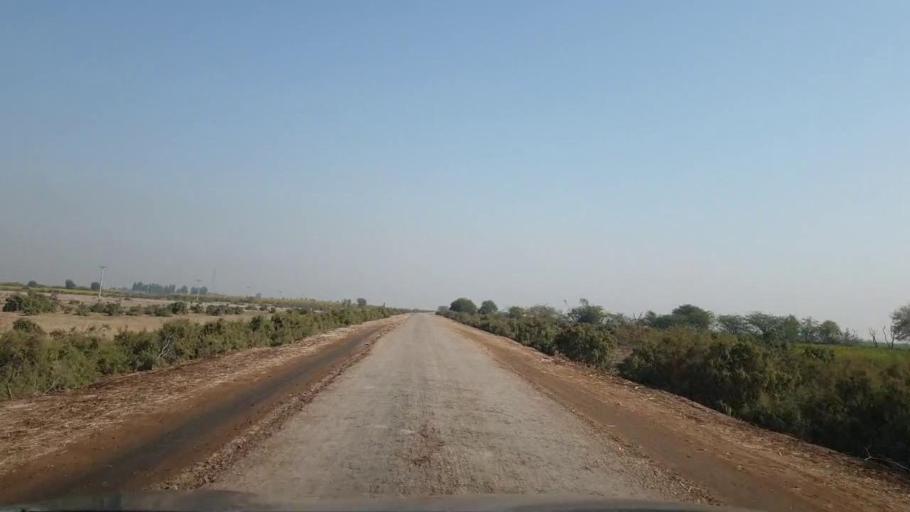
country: PK
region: Sindh
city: Berani
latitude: 25.6338
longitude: 68.8650
